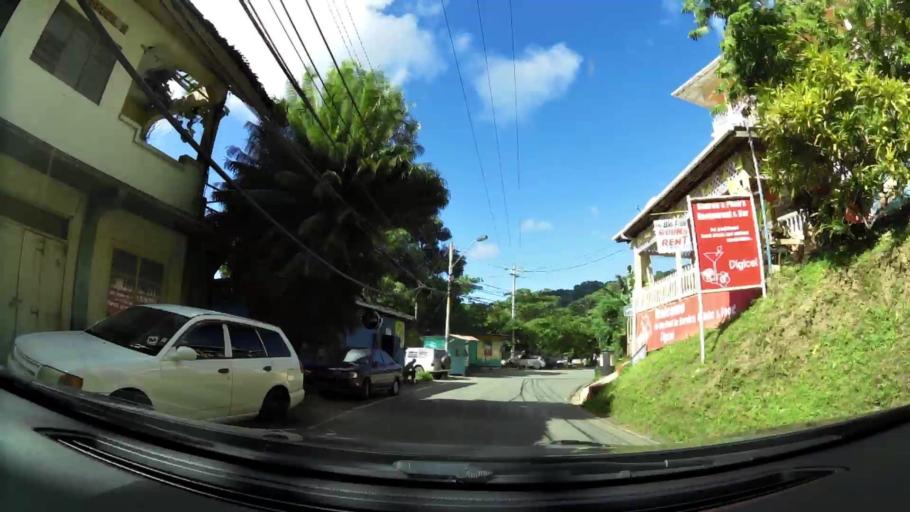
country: TT
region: Eastern Tobago
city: Roxborough
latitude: 11.3216
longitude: -60.5497
